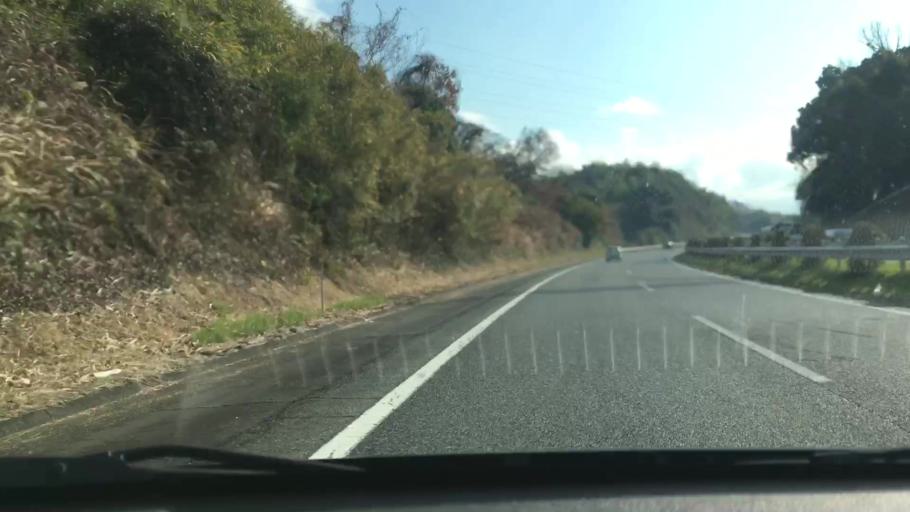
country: JP
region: Kumamoto
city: Matsubase
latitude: 32.6359
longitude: 130.7100
